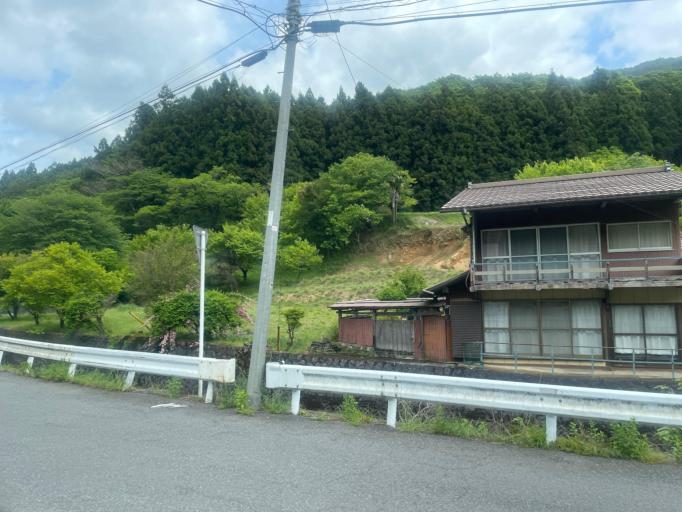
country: JP
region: Tochigi
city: Tanuma
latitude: 36.4724
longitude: 139.5954
